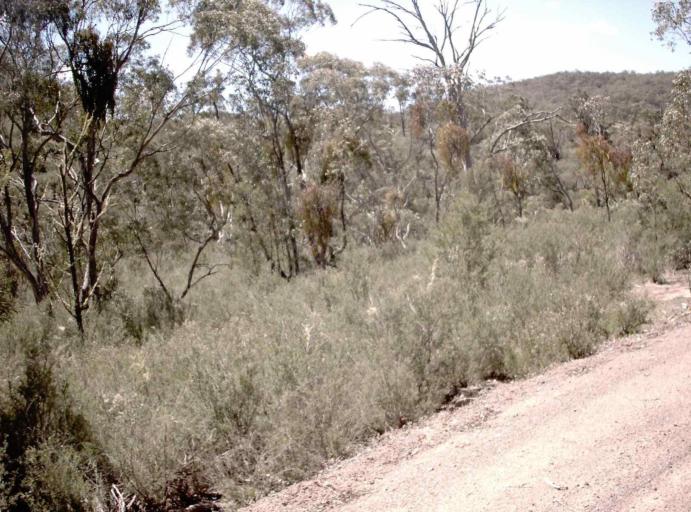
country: AU
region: New South Wales
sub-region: Snowy River
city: Jindabyne
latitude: -37.0377
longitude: 148.5380
